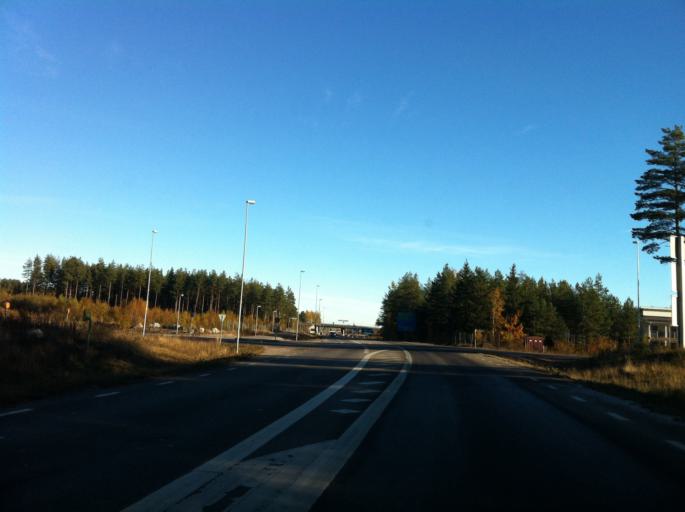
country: SE
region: Gaevleborg
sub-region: Gavle Kommun
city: Gavle
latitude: 60.6355
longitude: 17.1340
